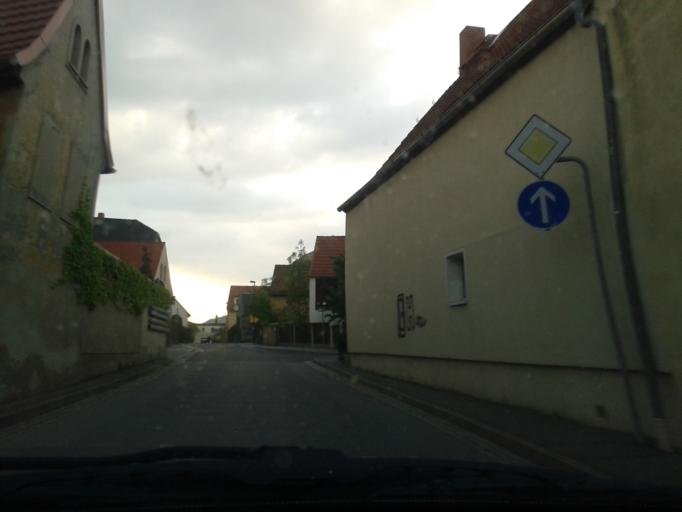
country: DE
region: Saxony
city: Radebeul
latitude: 51.0966
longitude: 13.6764
